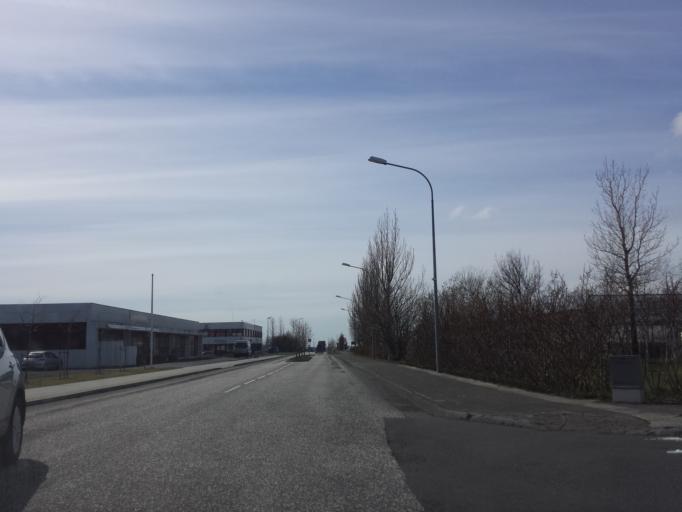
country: IS
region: South
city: Hveragerdi
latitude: 63.9984
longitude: -21.1886
